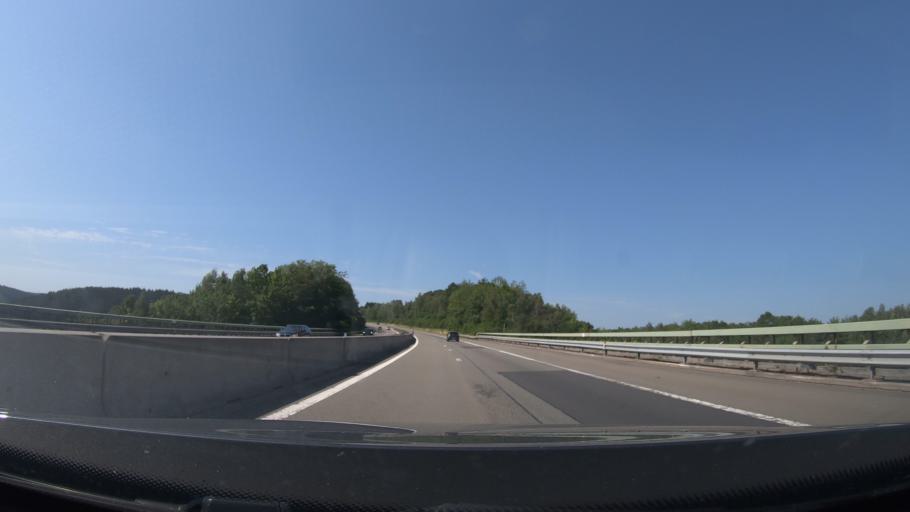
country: BE
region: Wallonia
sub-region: Province de Liege
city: Malmedy
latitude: 50.4154
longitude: 5.9923
